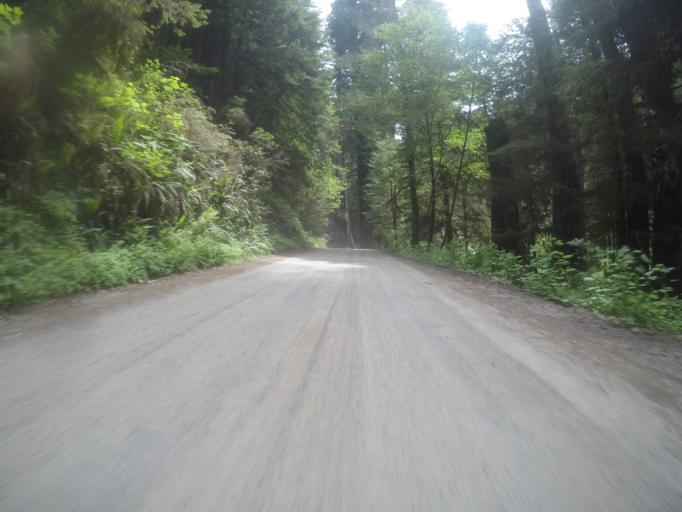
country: US
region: California
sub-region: Del Norte County
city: Bertsch-Oceanview
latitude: 41.7652
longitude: -124.1214
